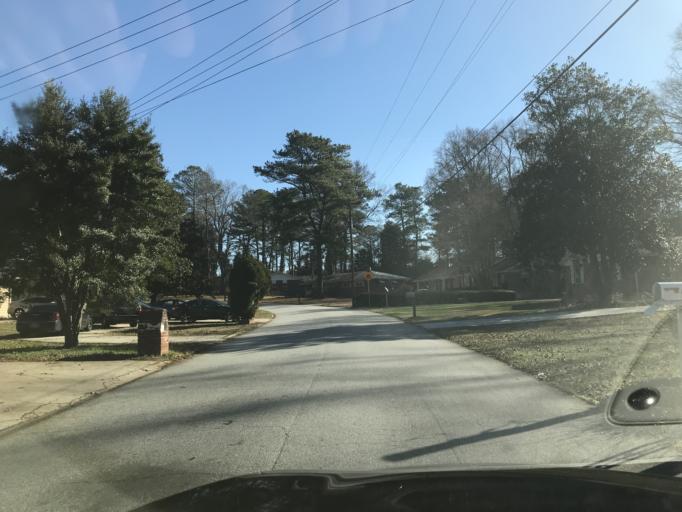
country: US
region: Georgia
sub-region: Clayton County
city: Riverdale
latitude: 33.5727
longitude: -84.3758
